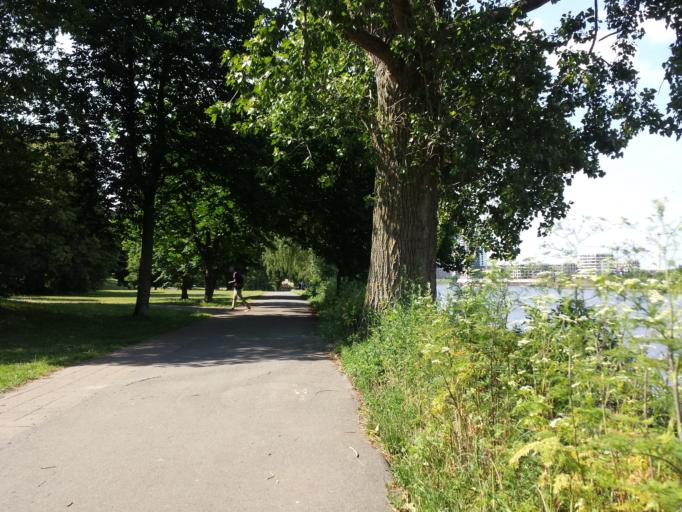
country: DE
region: Bremen
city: Bremen
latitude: 53.0899
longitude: 8.7635
